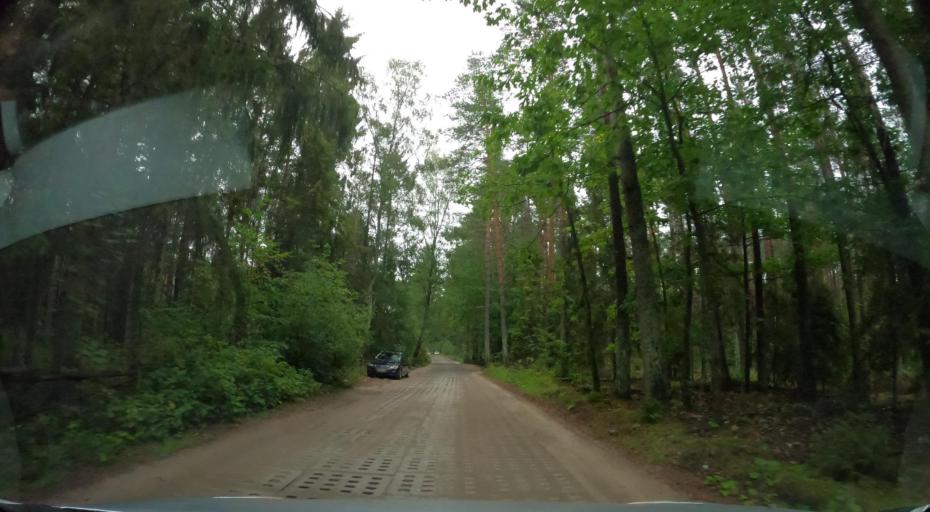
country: PL
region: Pomeranian Voivodeship
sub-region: Powiat kartuski
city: Chwaszczyno
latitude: 54.4187
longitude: 18.4276
